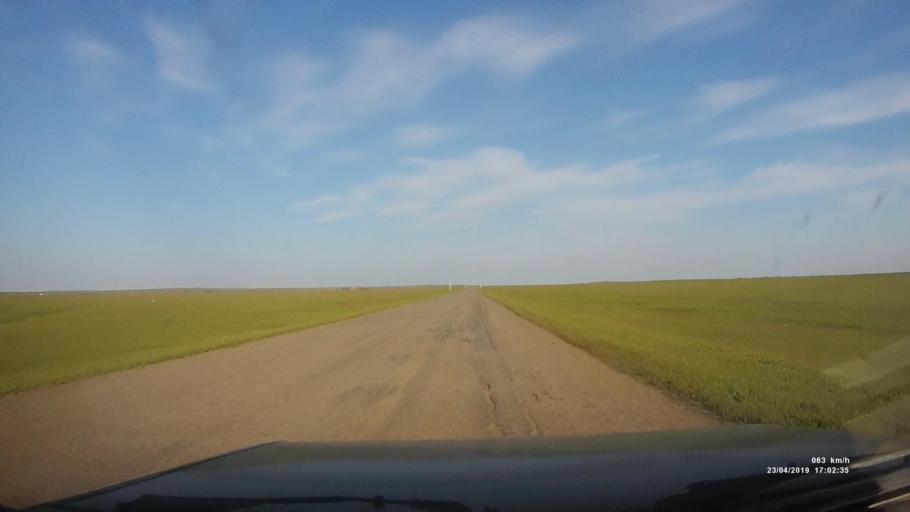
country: RU
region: Kalmykiya
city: Priyutnoye
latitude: 46.2922
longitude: 43.4196
